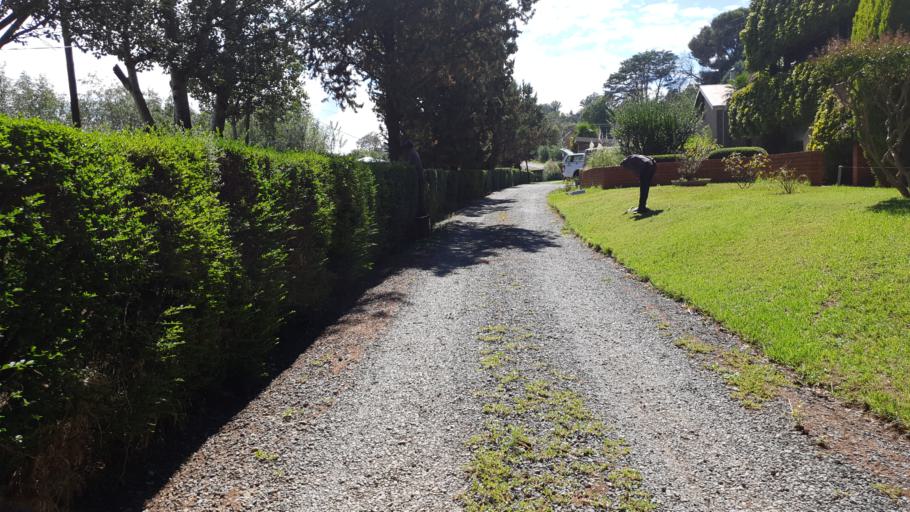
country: LS
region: Maseru
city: Nako
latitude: -29.6253
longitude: 27.5065
